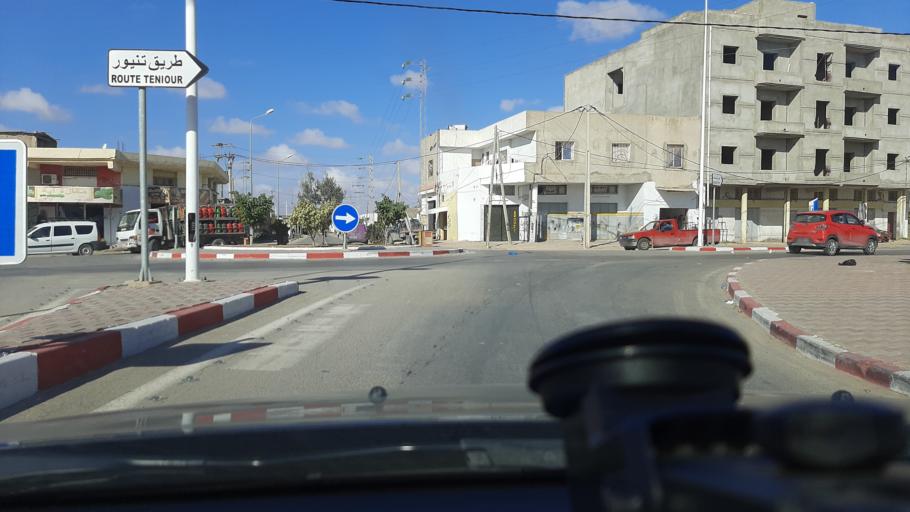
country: TN
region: Safaqis
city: Sfax
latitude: 34.8114
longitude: 10.7101
